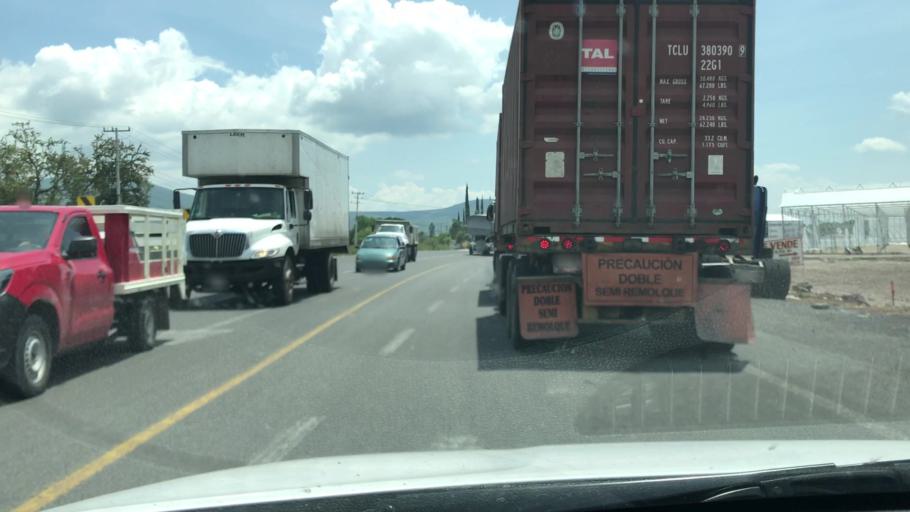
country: MX
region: Michoacan
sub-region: Yurecuaro
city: Yurecuaro
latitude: 20.3189
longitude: -102.3024
